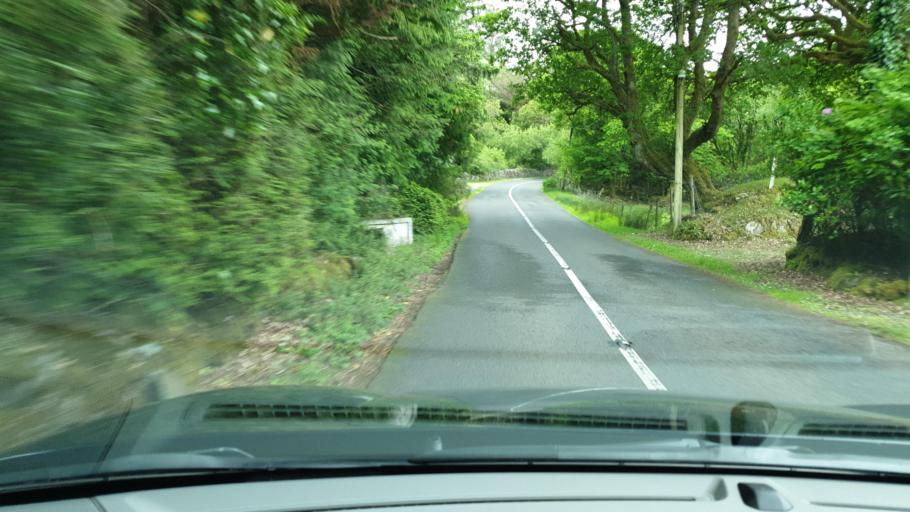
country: IE
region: Connaught
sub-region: County Galway
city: Clifden
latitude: 53.4581
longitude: -9.8200
